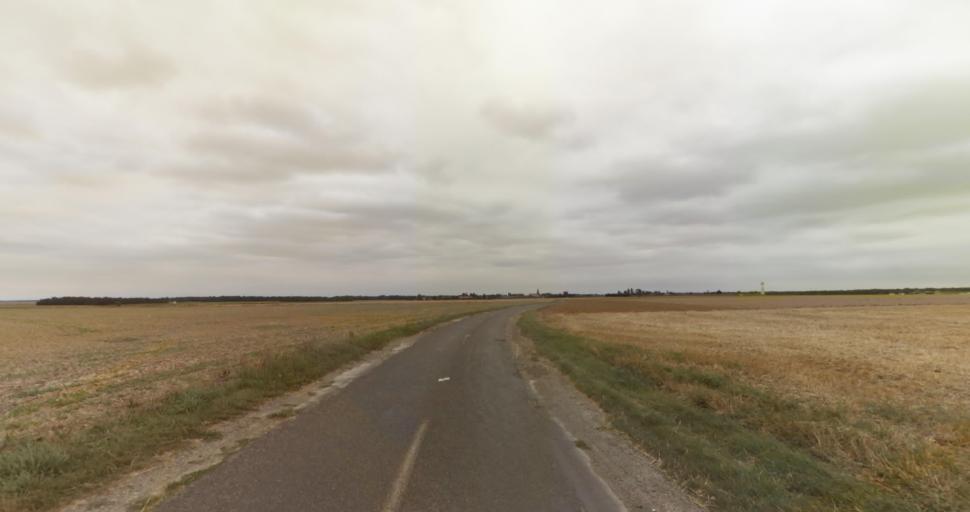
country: FR
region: Haute-Normandie
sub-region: Departement de l'Eure
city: La Couture-Boussey
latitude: 48.9179
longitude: 1.3370
